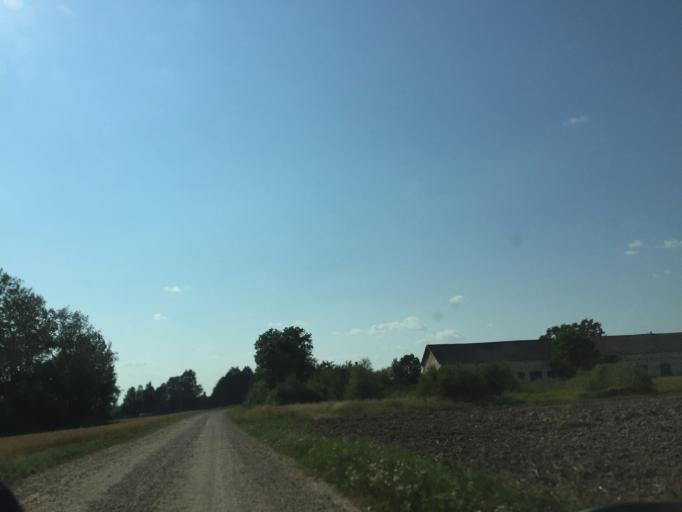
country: LV
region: Jelgava
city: Jelgava
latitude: 56.4555
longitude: 23.7062
